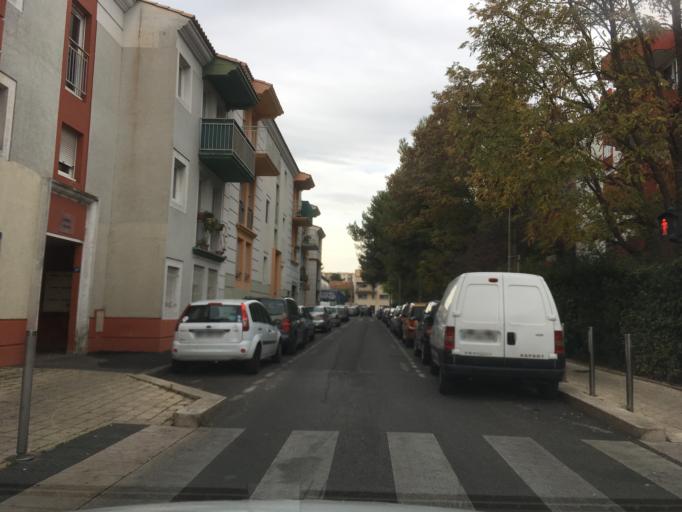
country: FR
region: Languedoc-Roussillon
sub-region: Departement de l'Herault
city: Montpellier
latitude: 43.6175
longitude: 3.8839
